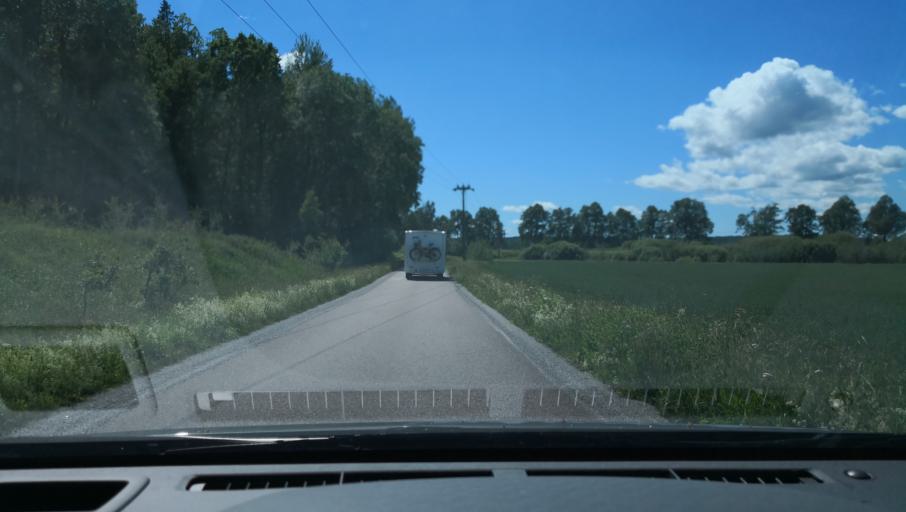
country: SE
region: Vaestmanland
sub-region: Arboga Kommun
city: Tyringe
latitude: 59.3995
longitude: 15.9347
